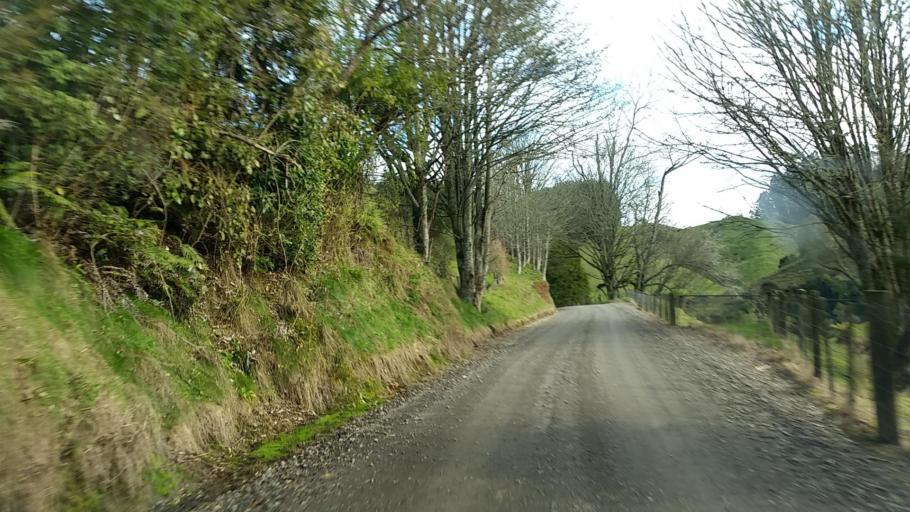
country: NZ
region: Taranaki
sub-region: New Plymouth District
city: Waitara
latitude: -39.1624
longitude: 174.5745
